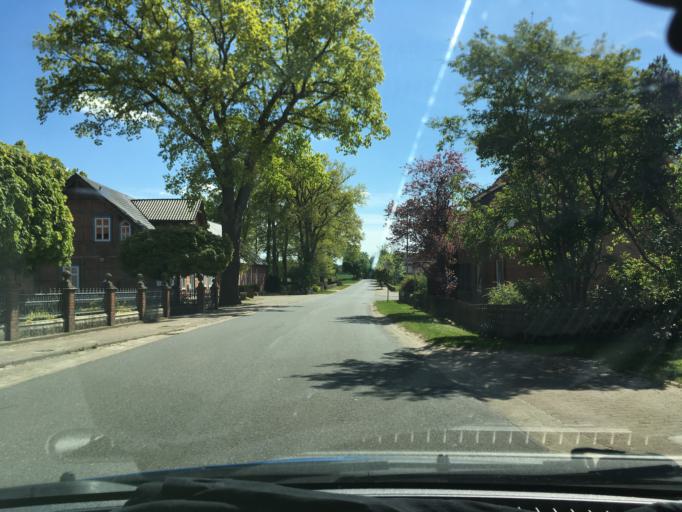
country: DE
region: Lower Saxony
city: Zernien
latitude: 53.0497
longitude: 10.8775
